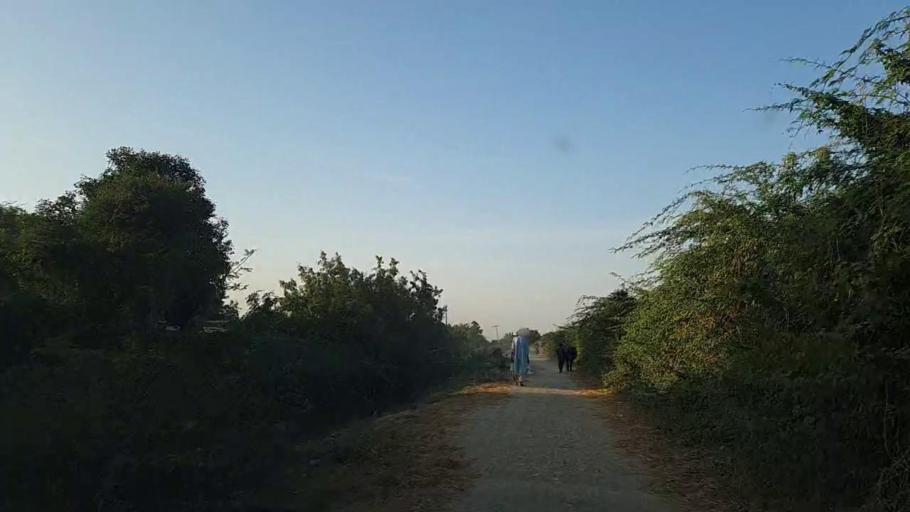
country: PK
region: Sindh
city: Mirpur Batoro
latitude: 24.7080
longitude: 68.2156
